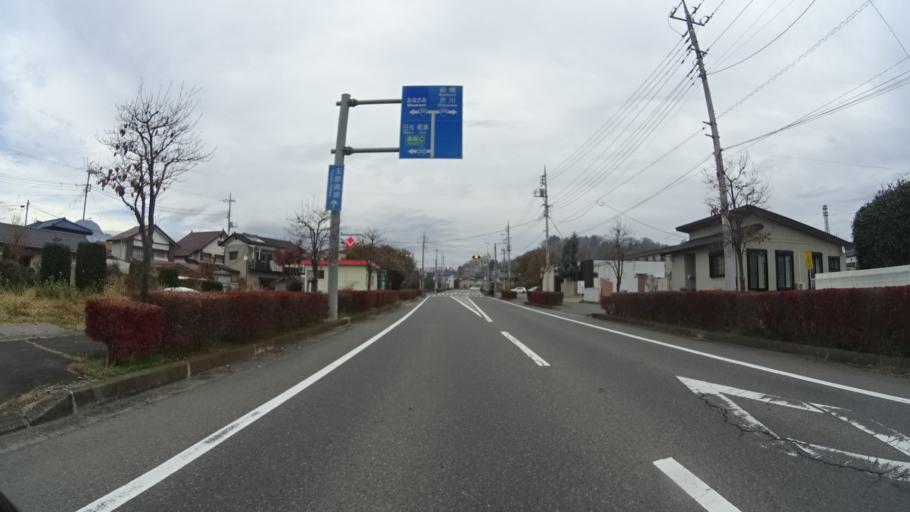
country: JP
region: Gunma
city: Numata
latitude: 36.6456
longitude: 139.0302
